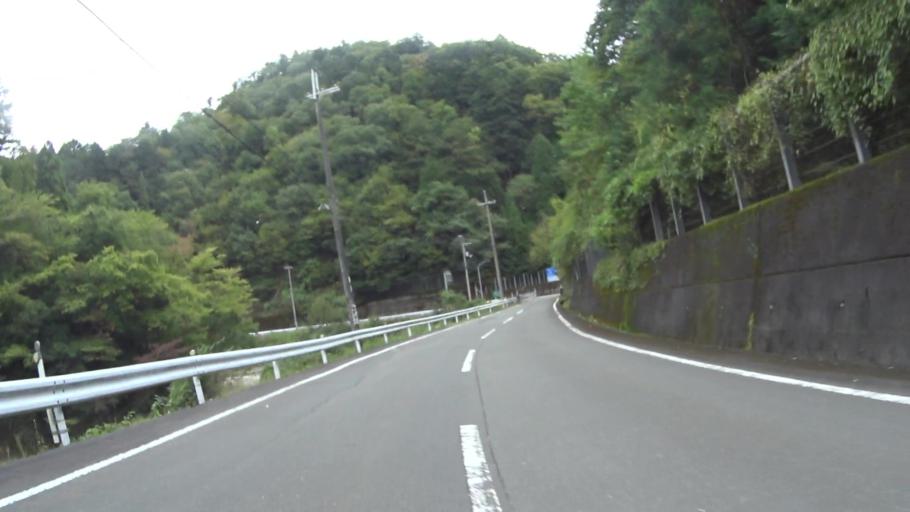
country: JP
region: Fukui
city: Obama
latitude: 35.3030
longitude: 135.6995
